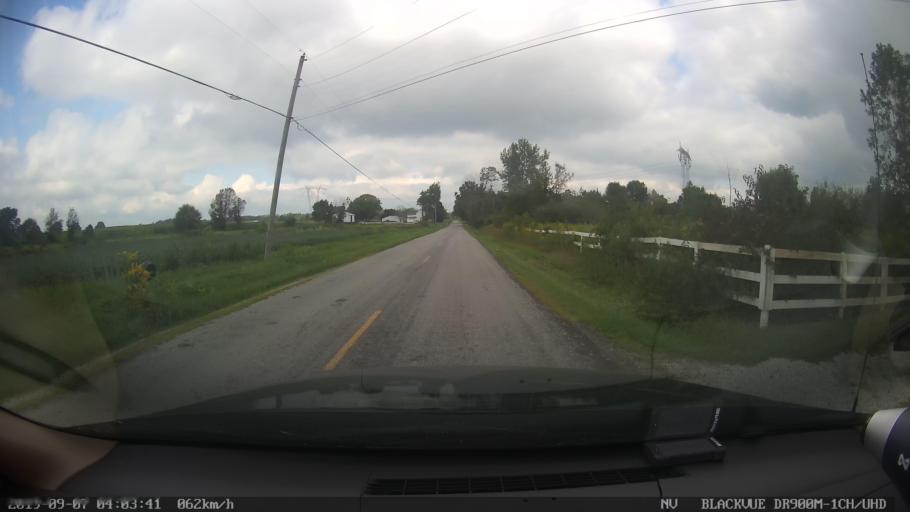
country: US
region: Ohio
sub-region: Licking County
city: Johnstown
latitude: 40.1877
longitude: -82.5934
